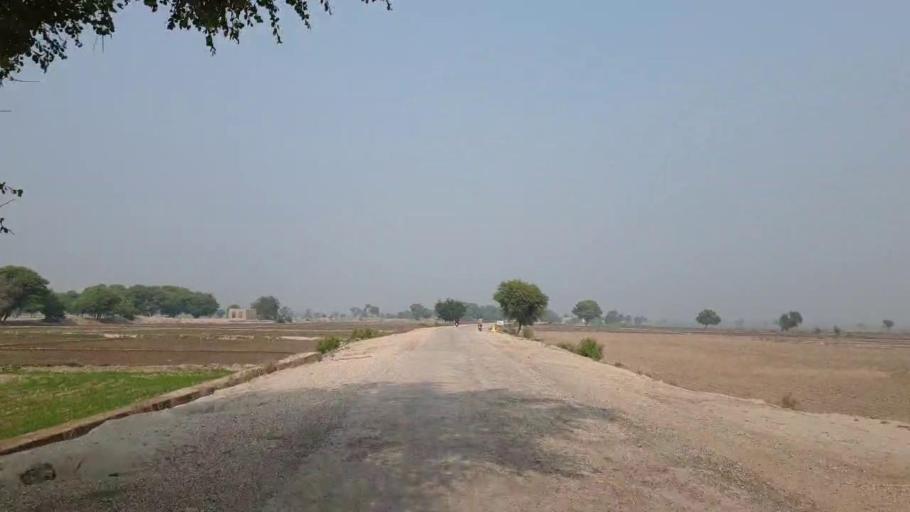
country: PK
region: Sindh
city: Bhan
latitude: 26.5191
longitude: 67.6898
